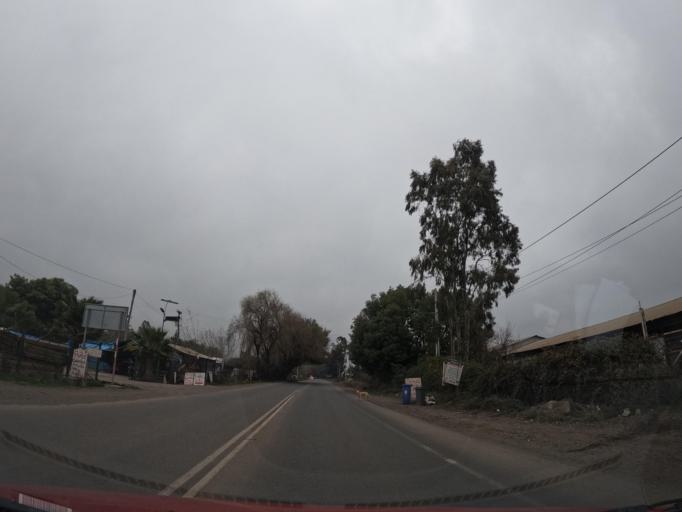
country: CL
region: Maule
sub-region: Provincia de Talca
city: San Clemente
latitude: -35.5524
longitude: -71.4696
